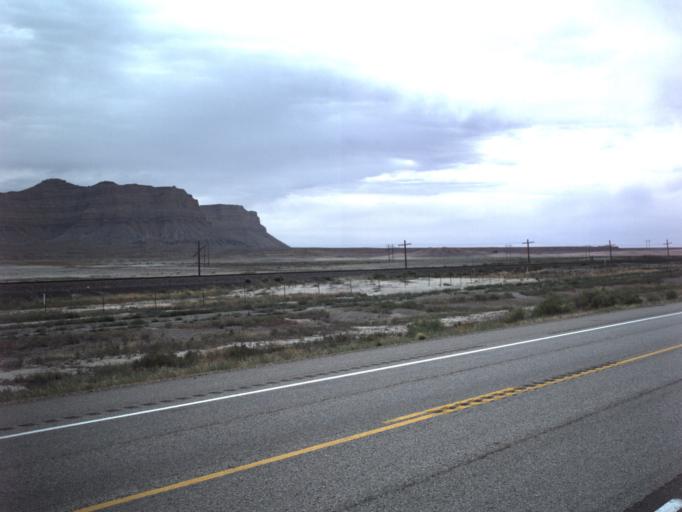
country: US
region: Utah
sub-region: Carbon County
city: East Carbon City
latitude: 39.1100
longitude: -110.3267
